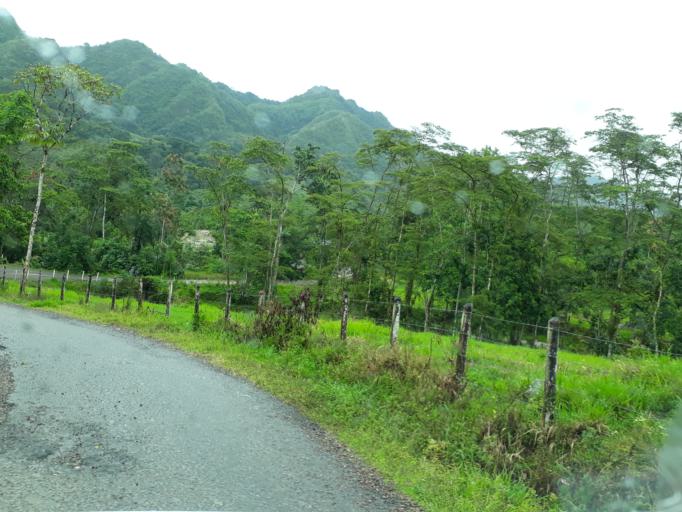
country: CO
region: Boyaca
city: Santa Maria
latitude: 4.7016
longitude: -73.3029
